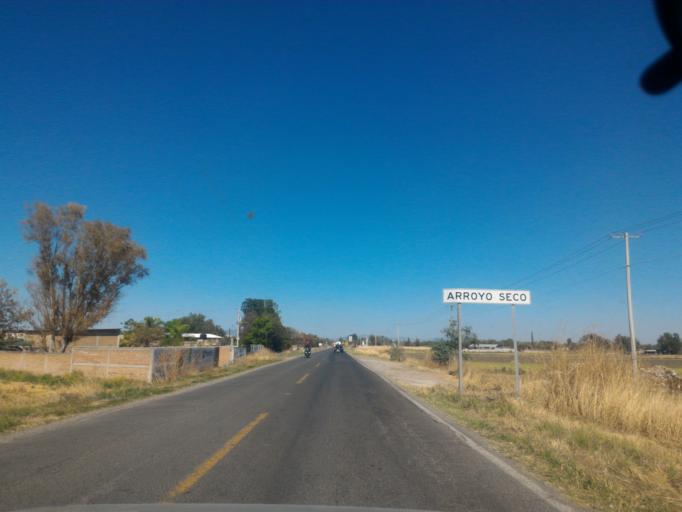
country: MX
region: Guanajuato
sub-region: San Francisco del Rincon
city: San Roque de Montes
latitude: 20.9953
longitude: -101.8164
